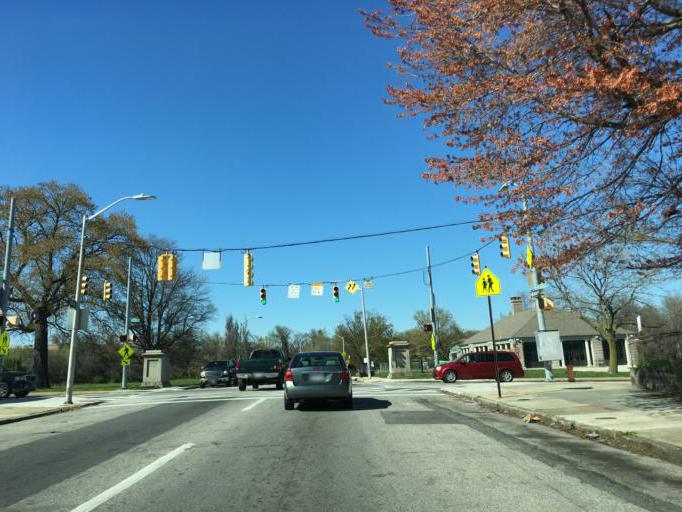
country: US
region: Maryland
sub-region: City of Baltimore
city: Baltimore
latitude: 39.3140
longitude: -76.5905
